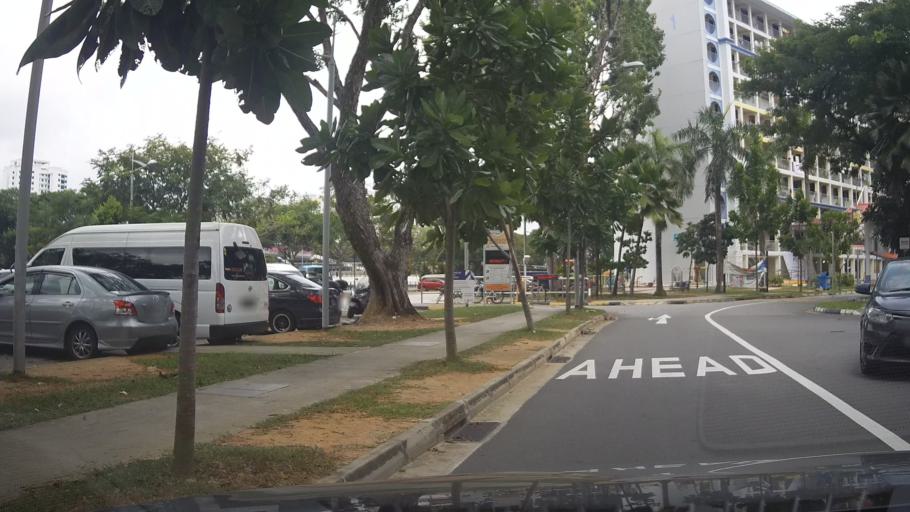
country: SG
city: Singapore
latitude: 1.3031
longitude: 103.8830
